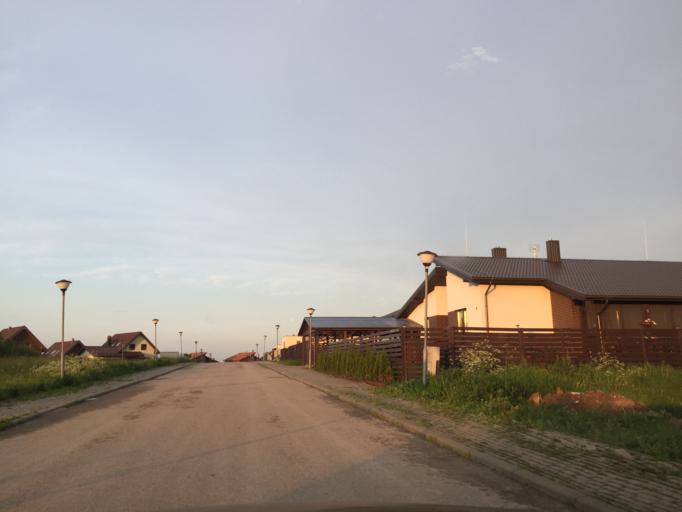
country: LT
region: Klaipedos apskritis
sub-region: Klaipeda
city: Klaipeda
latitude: 55.7576
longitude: 21.1549
